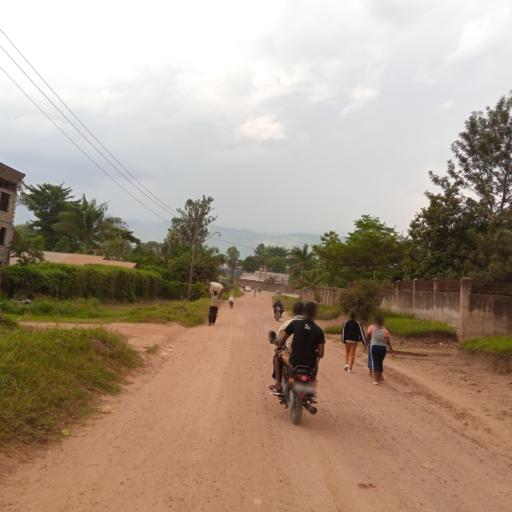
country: UG
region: Eastern Region
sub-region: Mbale District
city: Mbale
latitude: 1.0828
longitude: 34.1748
